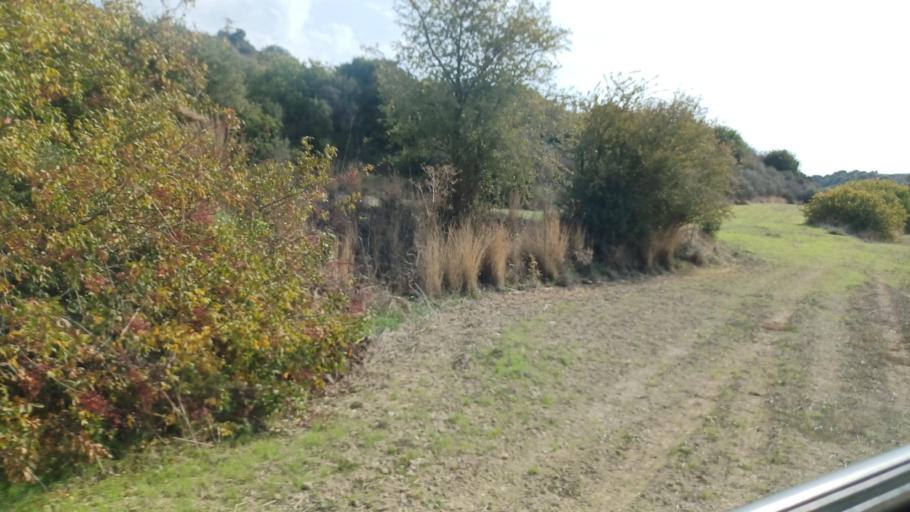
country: CY
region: Pafos
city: Polis
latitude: 34.9727
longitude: 32.4549
